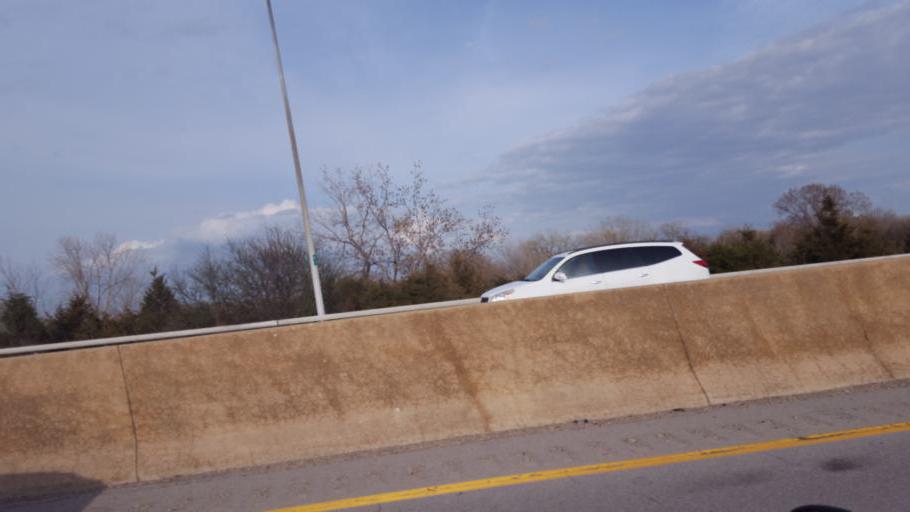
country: US
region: Ohio
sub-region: Ottawa County
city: Port Clinton
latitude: 41.4991
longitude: -82.8368
